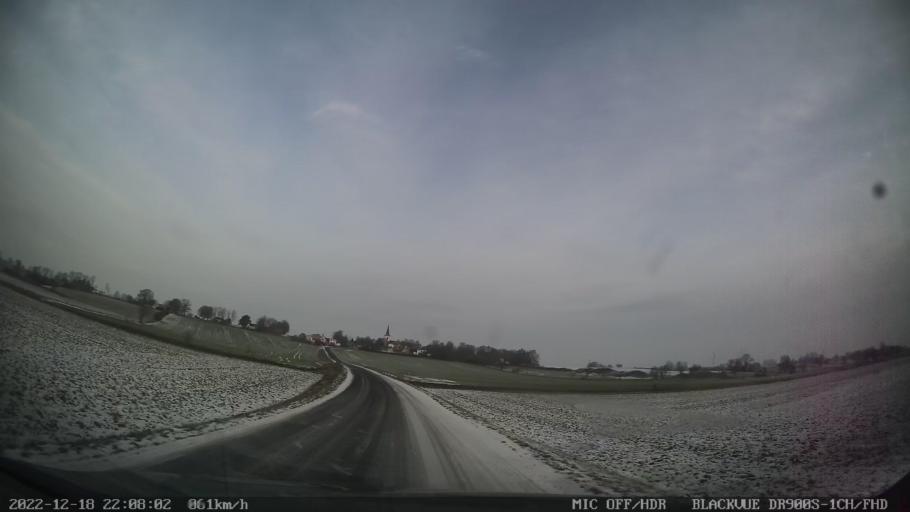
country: SE
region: Skane
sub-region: Tomelilla Kommun
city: Tomelilla
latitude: 55.5225
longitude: 14.0431
